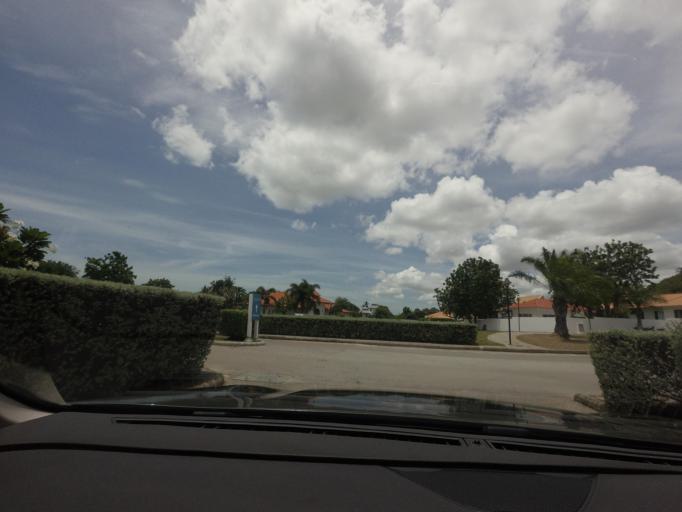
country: TH
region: Prachuap Khiri Khan
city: Hua Hin
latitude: 12.5158
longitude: 99.9603
